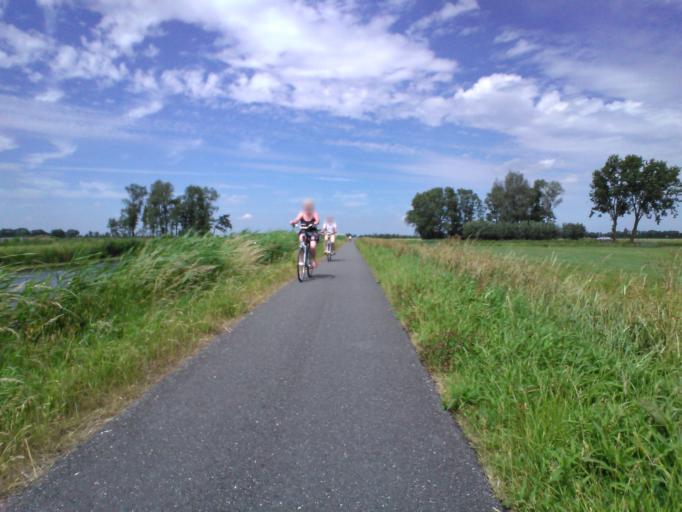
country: NL
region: South Holland
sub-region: Gemeente Giessenlanden
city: Giessenburg
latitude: 51.8681
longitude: 4.8793
